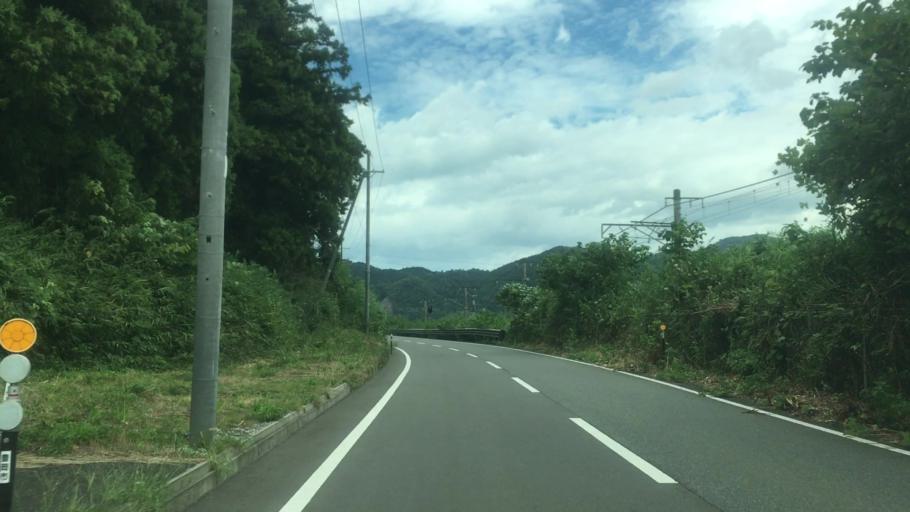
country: JP
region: Hyogo
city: Toyooka
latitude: 35.5717
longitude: 134.8046
